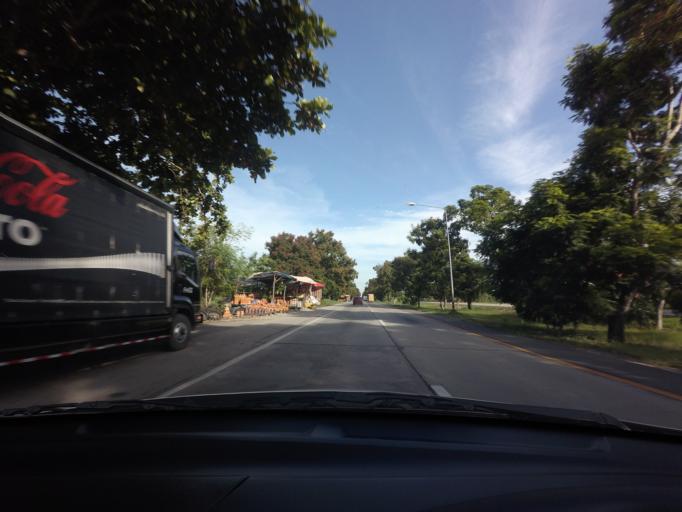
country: TH
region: Phra Nakhon Si Ayutthaya
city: Lat Bua Luang
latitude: 14.2369
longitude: 100.2707
